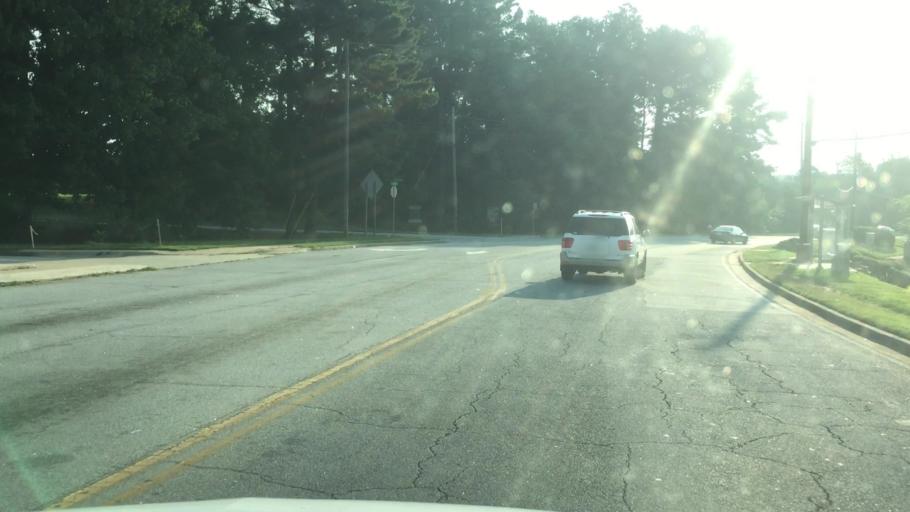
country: US
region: Georgia
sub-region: DeKalb County
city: Panthersville
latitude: 33.6930
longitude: -84.2603
